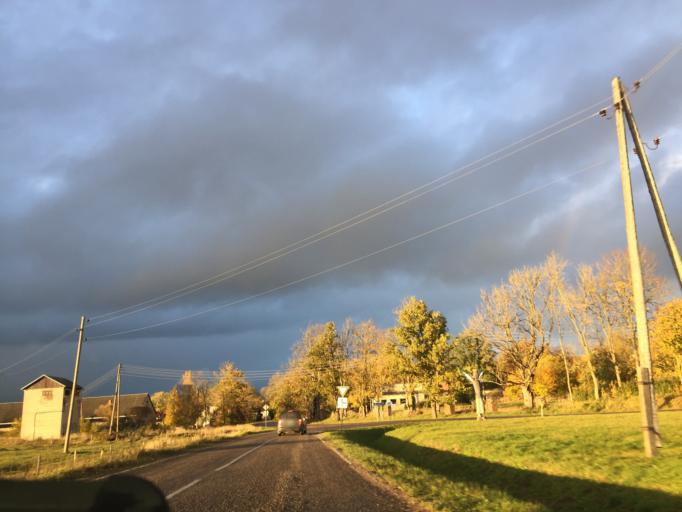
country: LV
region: Talsu Rajons
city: Sabile
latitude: 56.9475
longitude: 22.3994
